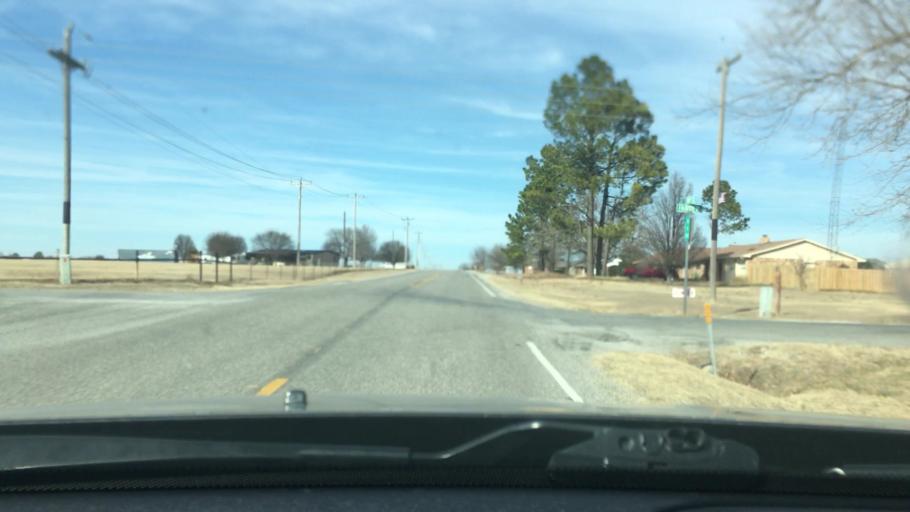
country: US
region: Oklahoma
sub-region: Murray County
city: Davis
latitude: 34.4953
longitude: -97.0904
